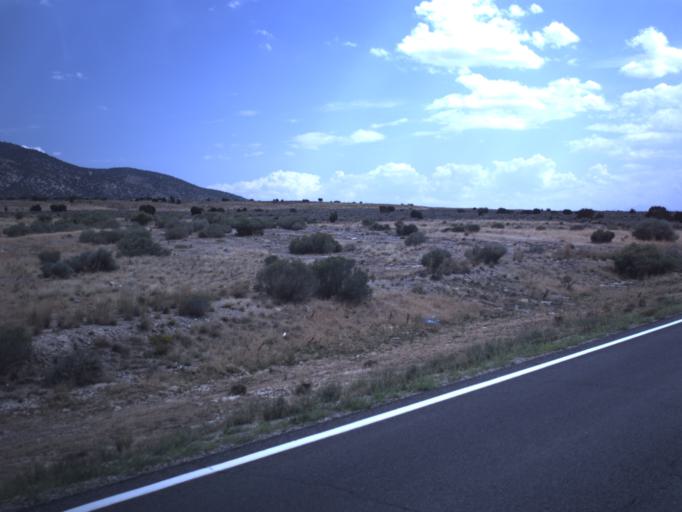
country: US
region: Utah
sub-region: Tooele County
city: Tooele
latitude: 40.3054
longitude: -112.2788
